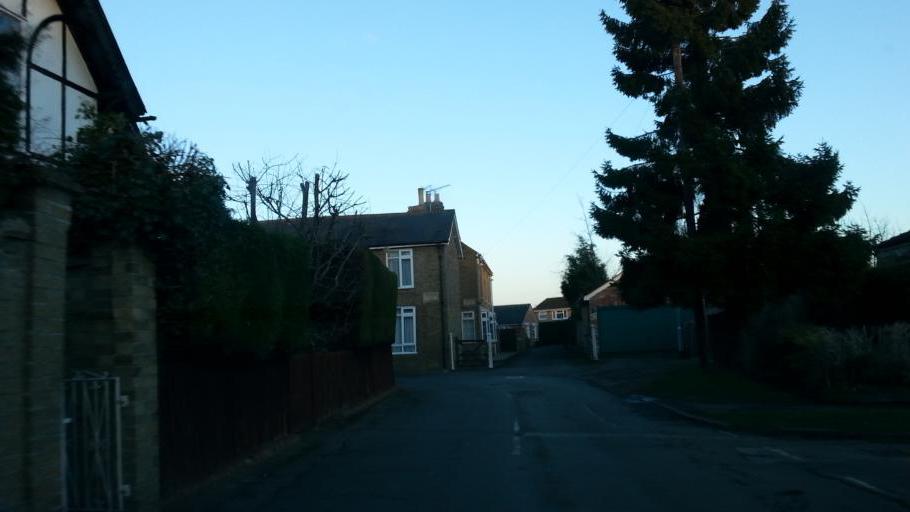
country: GB
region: England
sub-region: Cambridgeshire
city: Hemingford Grey
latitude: 52.2995
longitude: -0.0664
